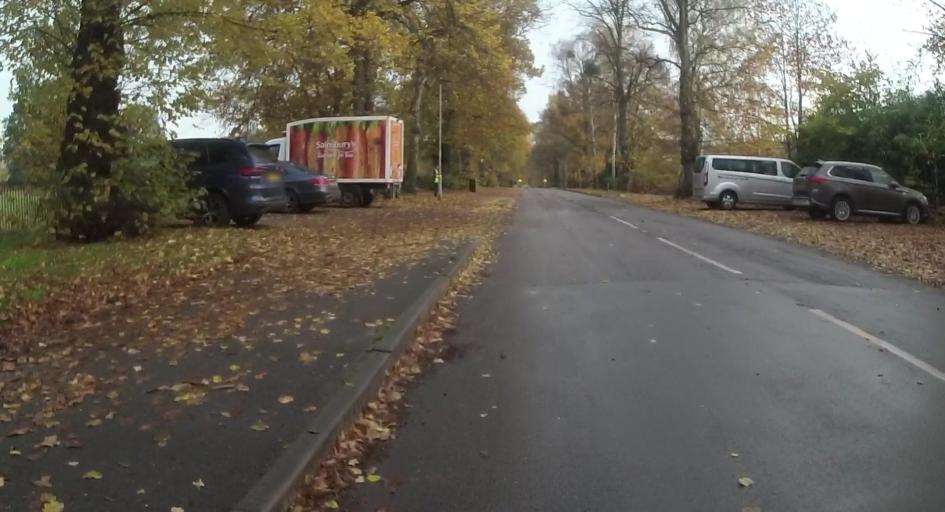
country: GB
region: England
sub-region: Bracknell Forest
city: Crowthorne
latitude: 51.3662
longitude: -0.7929
